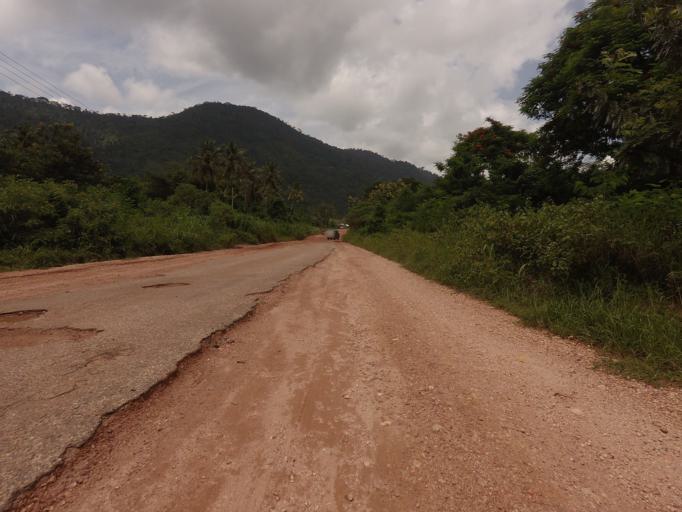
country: GH
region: Volta
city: Ho
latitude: 6.7668
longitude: 0.3639
